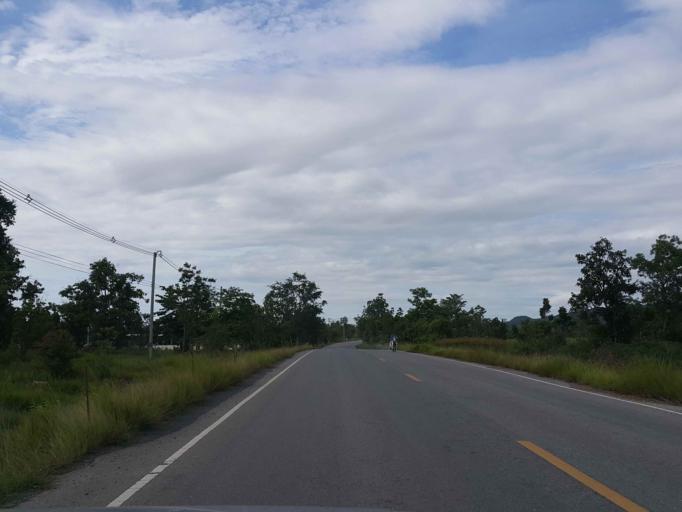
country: TH
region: Sukhothai
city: Thung Saliam
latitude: 17.2389
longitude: 99.5156
